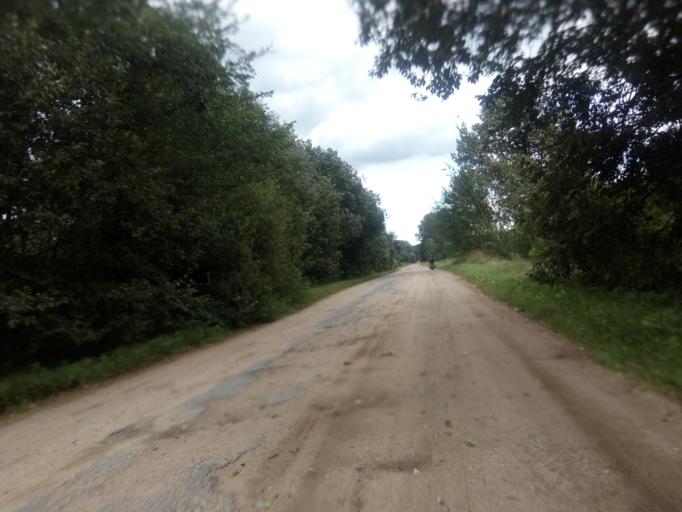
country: BY
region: Vitebsk
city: Dzisna
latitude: 55.7077
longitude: 28.3163
